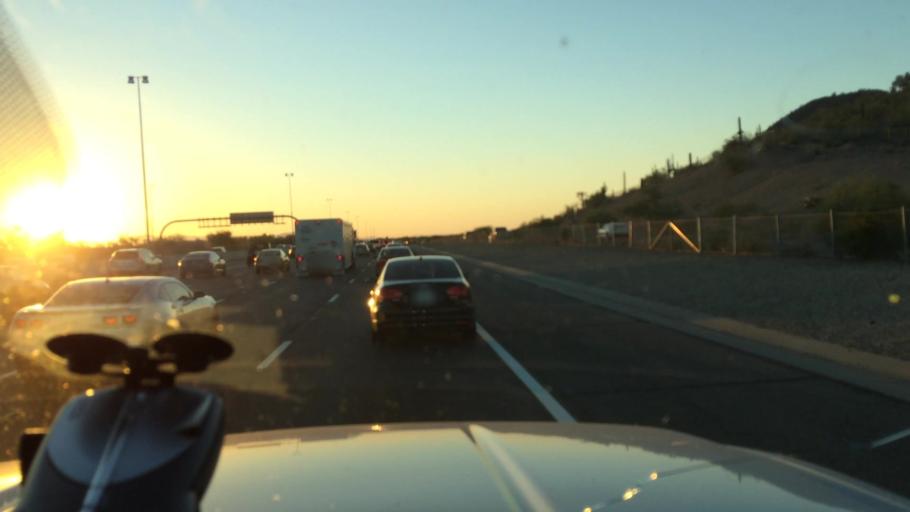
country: US
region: Arizona
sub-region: Maricopa County
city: Peoria
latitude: 33.6700
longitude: -112.1523
